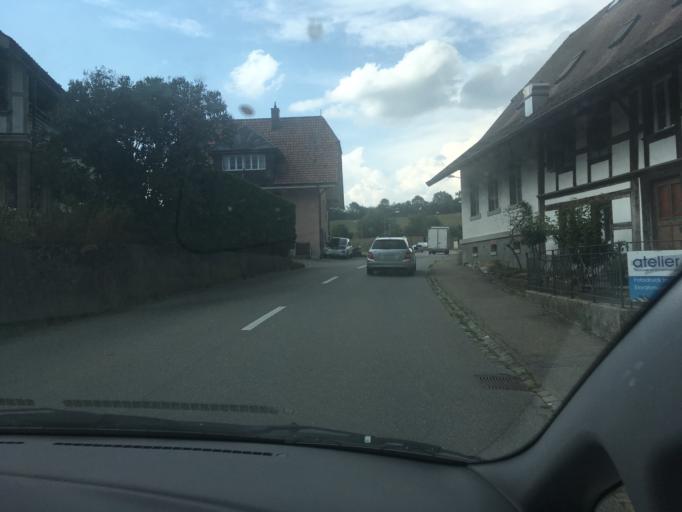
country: CH
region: Bern
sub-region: Bern-Mittelland District
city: Kirchlindach
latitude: 46.9941
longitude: 7.3981
